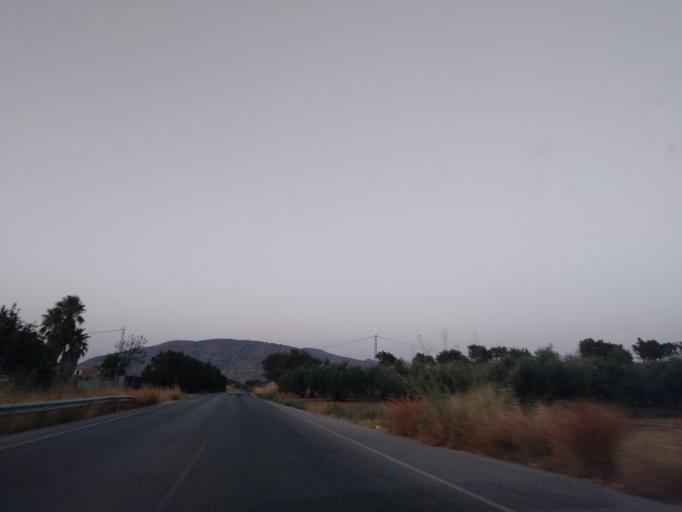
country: ES
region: Andalusia
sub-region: Provincia de Malaga
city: Cartama
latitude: 36.6772
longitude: -4.6596
